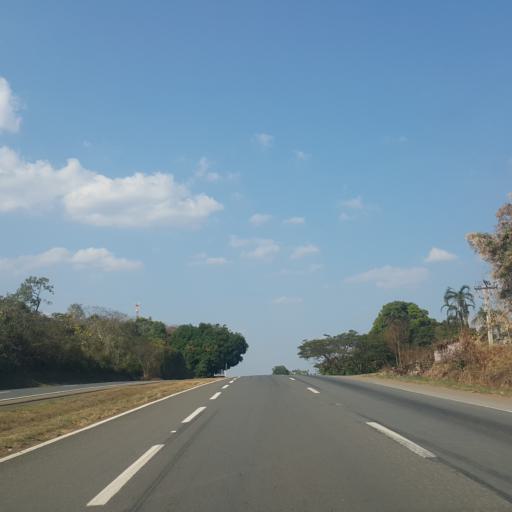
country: BR
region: Goias
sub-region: Abadiania
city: Abadiania
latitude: -16.1622
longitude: -48.6224
